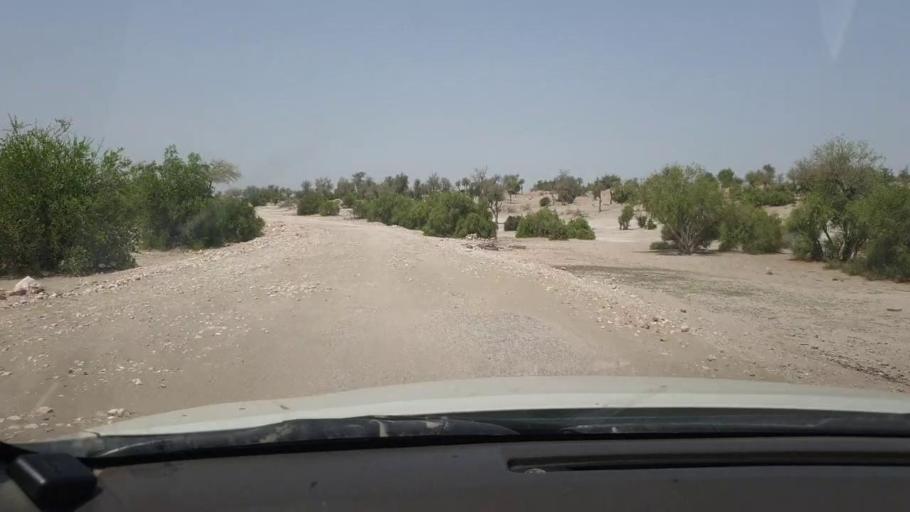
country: PK
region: Sindh
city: Rohri
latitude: 27.3251
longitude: 69.2796
